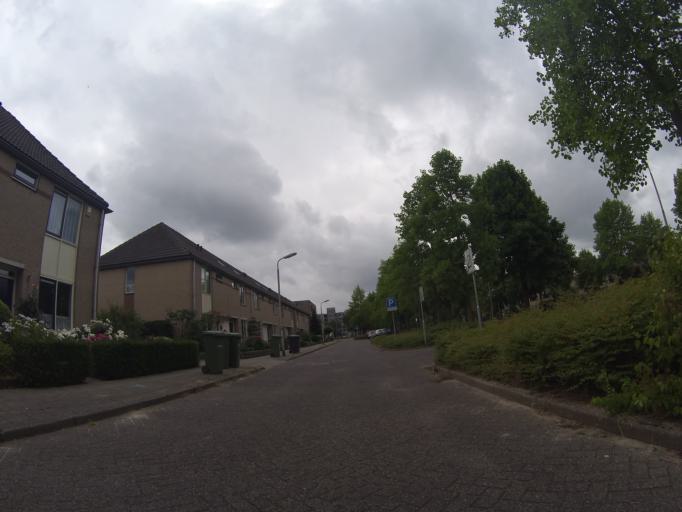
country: NL
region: Utrecht
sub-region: Gemeente Amersfoort
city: Amersfoort
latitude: 52.1799
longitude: 5.4029
